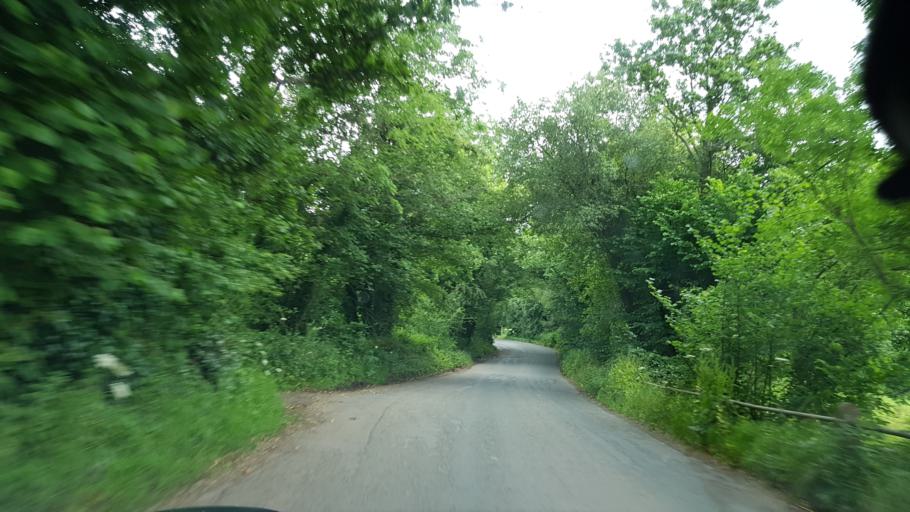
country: GB
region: England
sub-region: Herefordshire
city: Llancillo
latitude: 51.8818
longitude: -2.9722
